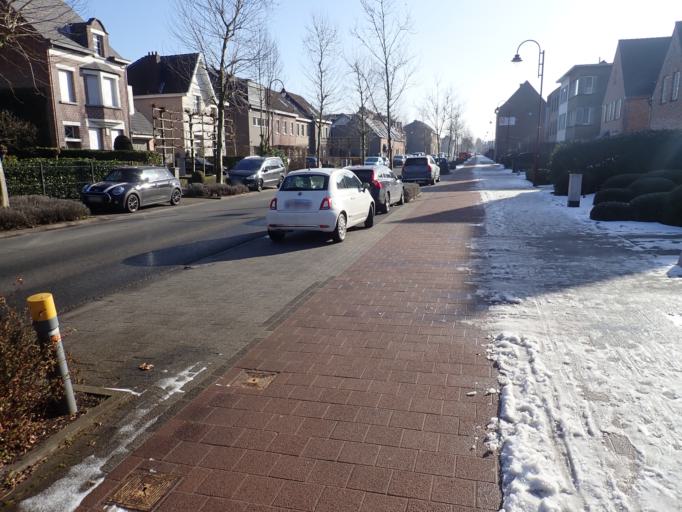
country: BE
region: Flanders
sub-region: Provincie Antwerpen
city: Boechout
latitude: 51.1674
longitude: 4.4816
